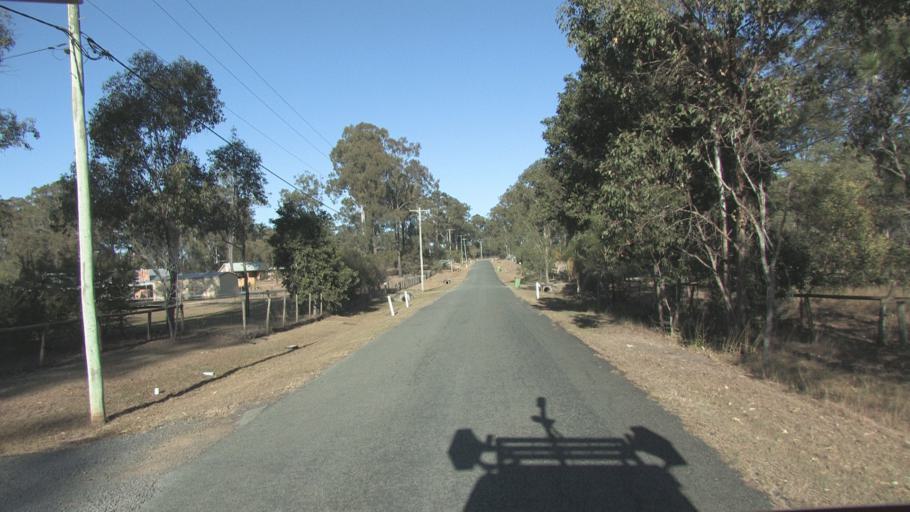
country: AU
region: Queensland
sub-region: Logan
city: Cedar Vale
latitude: -27.8377
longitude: 153.0143
